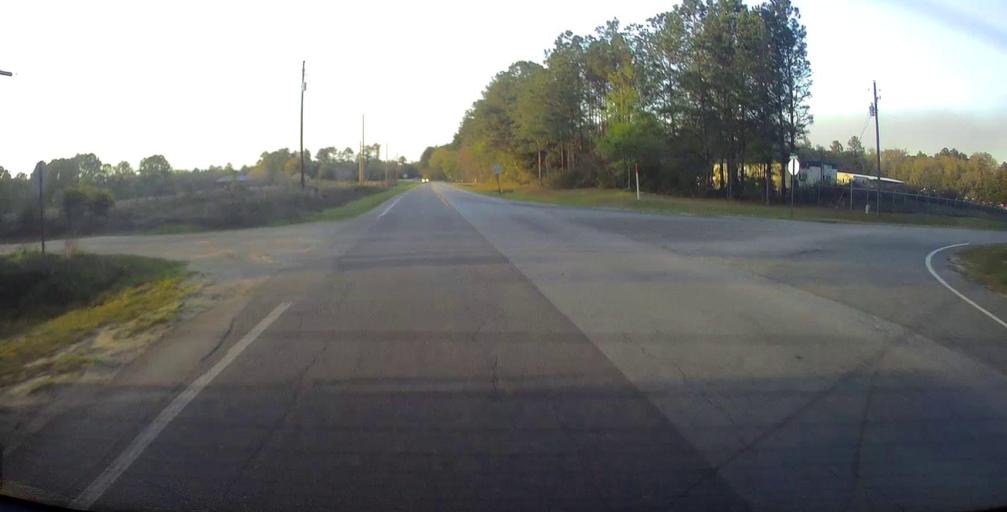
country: US
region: Georgia
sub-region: Chatham County
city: Bloomingdale
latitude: 32.1377
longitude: -81.3895
